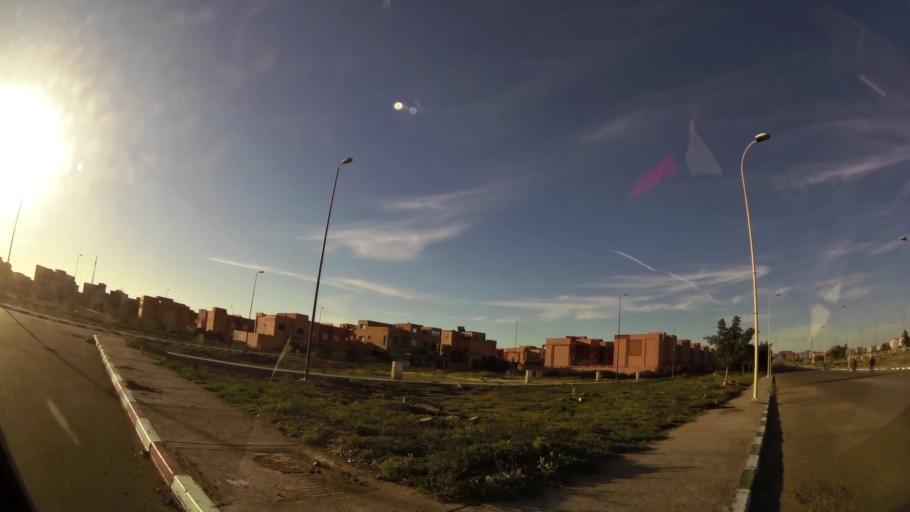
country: MA
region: Marrakech-Tensift-Al Haouz
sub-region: Marrakech
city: Marrakesh
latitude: 31.7587
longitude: -8.1096
